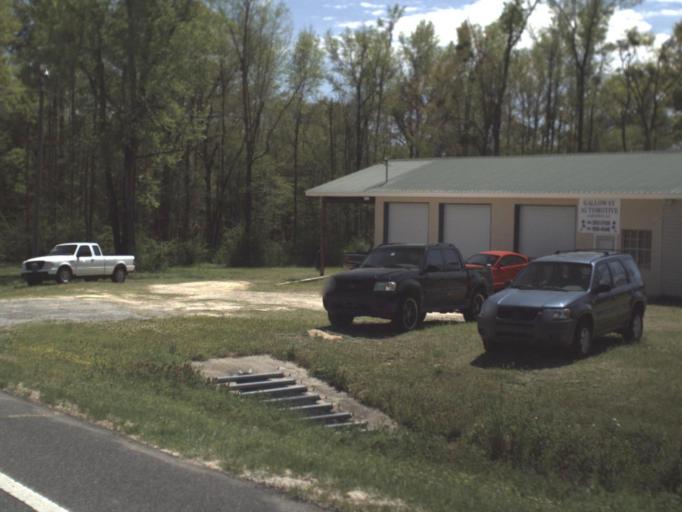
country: US
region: Alabama
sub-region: Geneva County
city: Geneva
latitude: 30.9523
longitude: -85.9847
